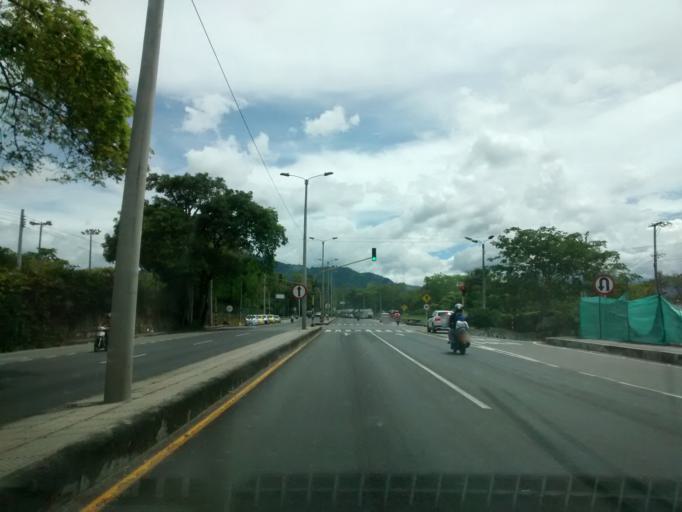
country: CO
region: Tolima
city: Ibague
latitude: 4.4044
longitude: -75.1597
